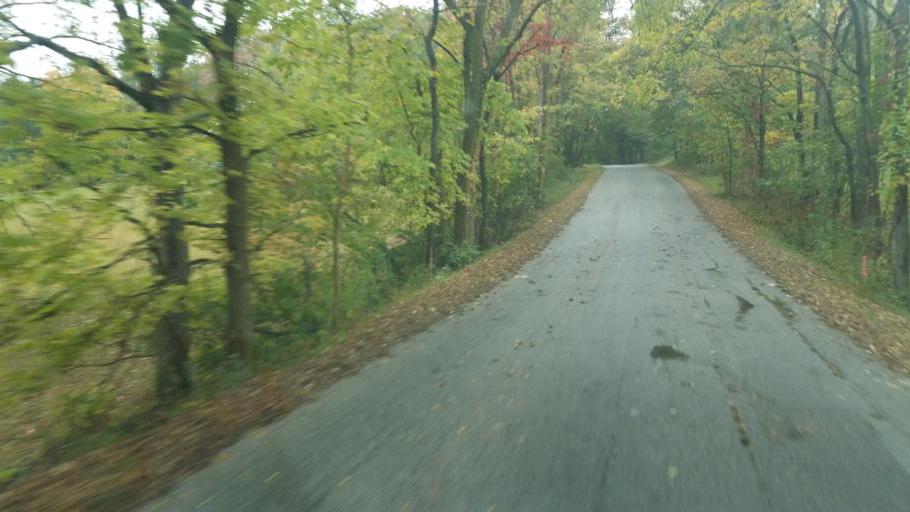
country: US
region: Ohio
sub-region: Ashland County
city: Loudonville
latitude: 40.6092
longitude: -82.2942
